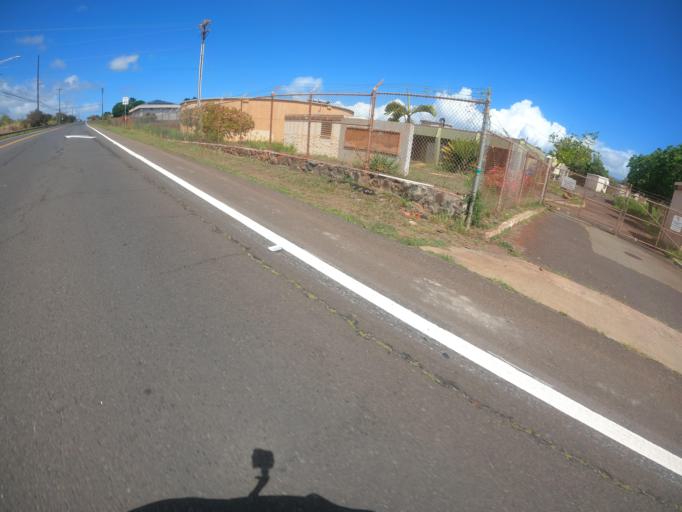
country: US
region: Hawaii
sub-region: Honolulu County
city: Village Park
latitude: 21.3984
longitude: -158.0388
